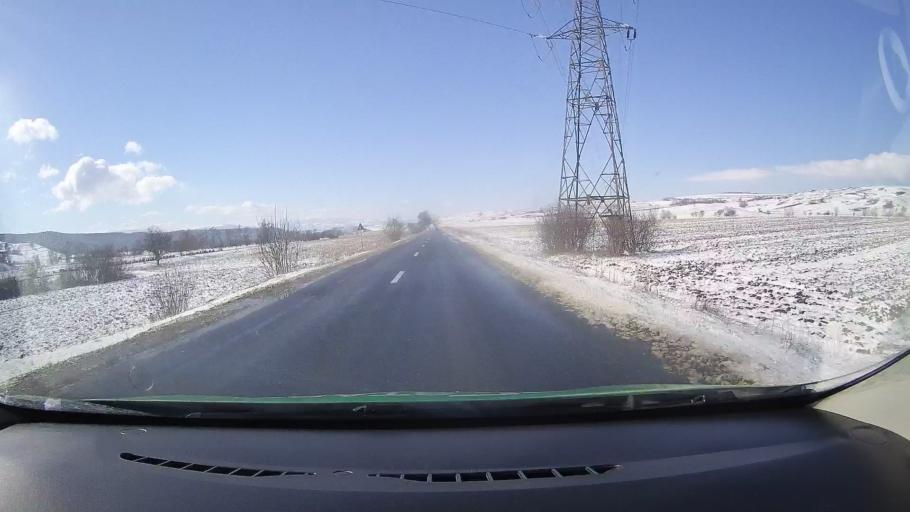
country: RO
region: Sibiu
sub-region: Comuna Rosia
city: Rosia
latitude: 45.7936
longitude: 24.3291
